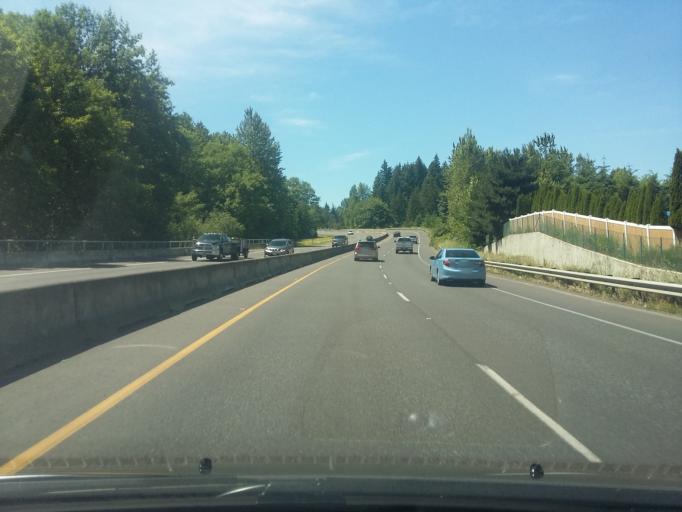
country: US
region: Washington
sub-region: Clark County
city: Five Corners
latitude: 45.6830
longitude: -122.5842
